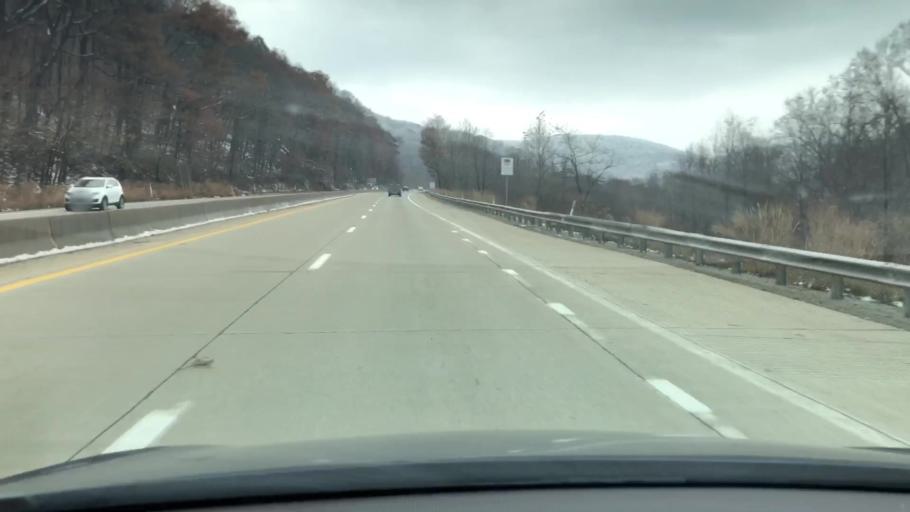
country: US
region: Pennsylvania
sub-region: Fayette County
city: Hopwood
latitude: 39.8673
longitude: -79.6896
